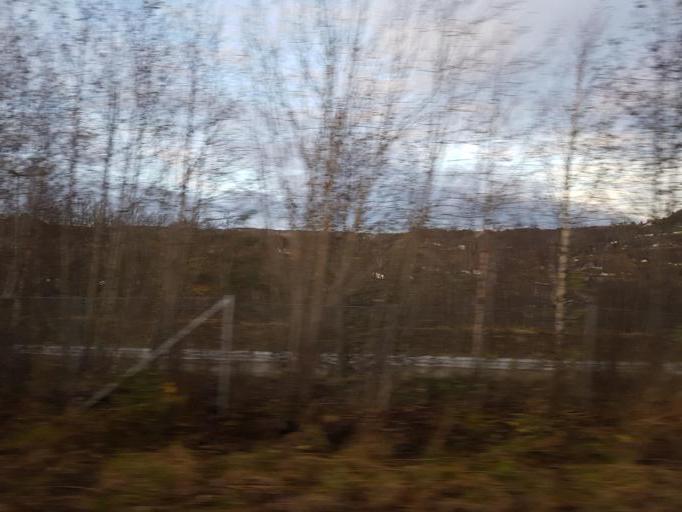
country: NO
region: Sor-Trondelag
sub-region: Melhus
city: Melhus
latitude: 63.2900
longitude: 10.2769
